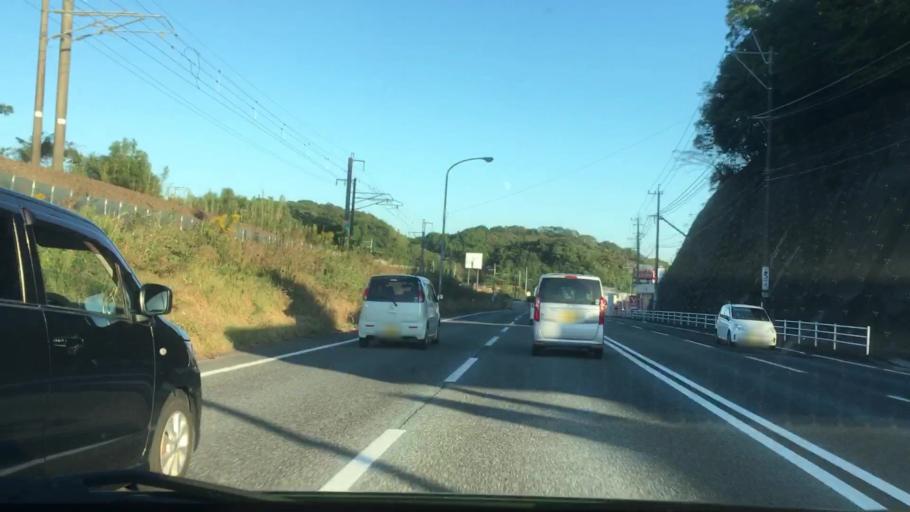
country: JP
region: Nagasaki
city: Sasebo
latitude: 33.1530
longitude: 129.7761
